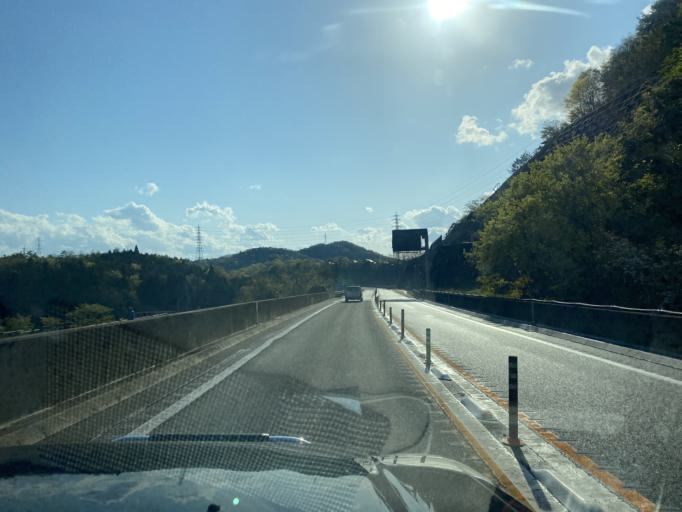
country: JP
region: Kyoto
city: Fukuchiyama
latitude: 35.2951
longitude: 135.1828
